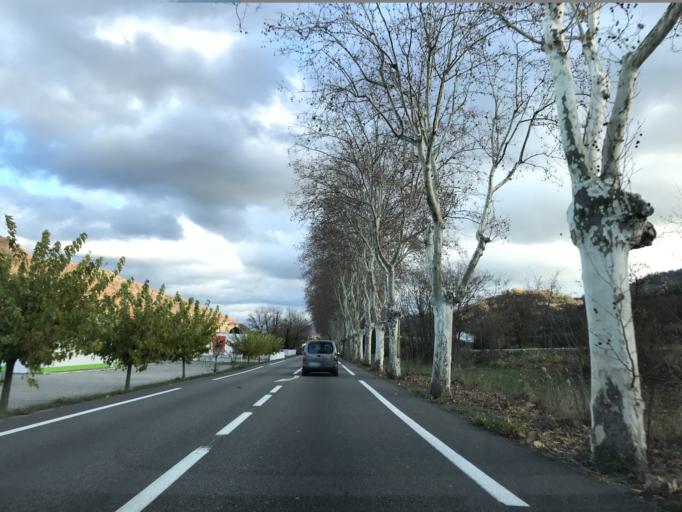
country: FR
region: Rhone-Alpes
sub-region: Departement de l'Ardeche
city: Privas
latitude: 44.7185
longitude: 4.6055
